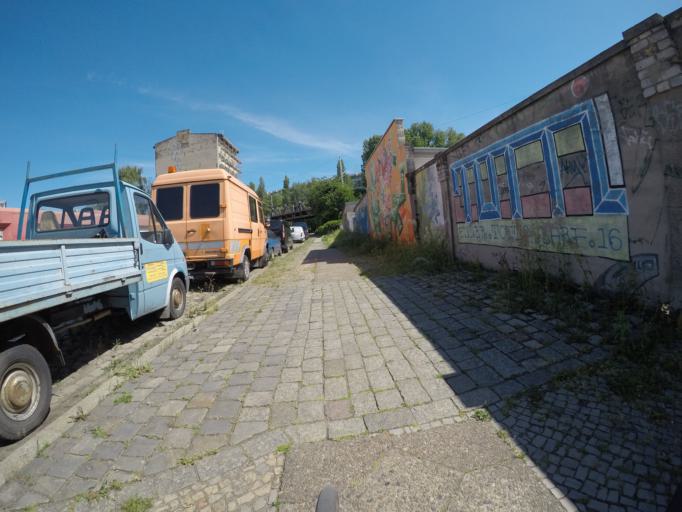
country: DE
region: Berlin
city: Rummelsburg
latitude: 52.5088
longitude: 13.4758
